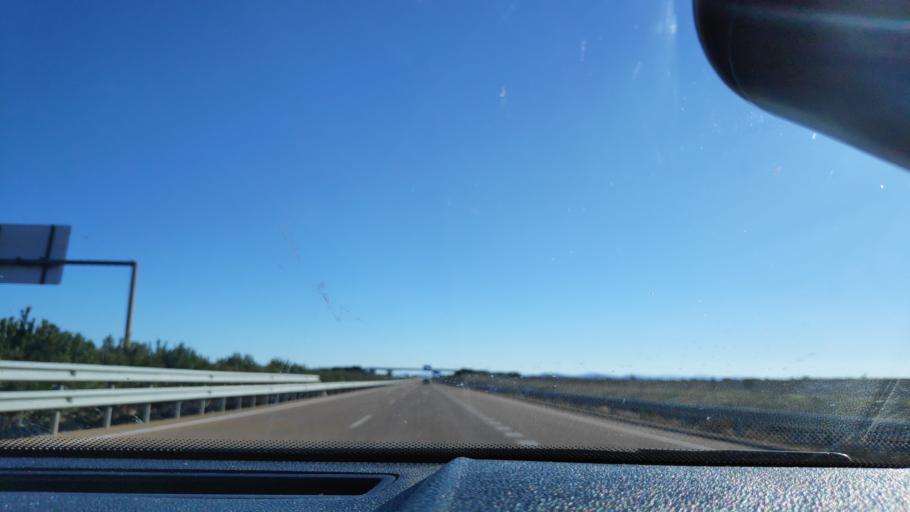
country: ES
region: Extremadura
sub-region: Provincia de Badajoz
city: Los Santos de Maimona
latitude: 38.4157
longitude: -6.3440
